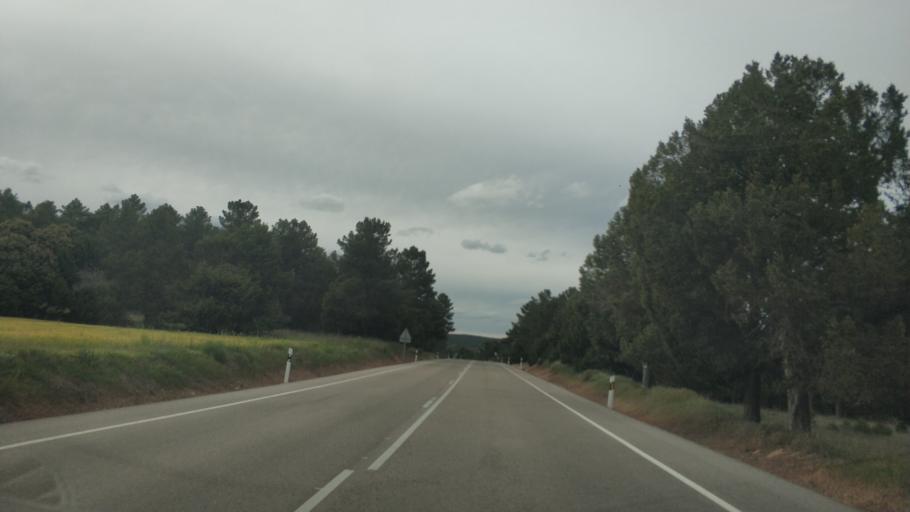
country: ES
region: Castille and Leon
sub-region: Provincia de Soria
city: Valdenebro
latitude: 41.5504
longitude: -2.9619
